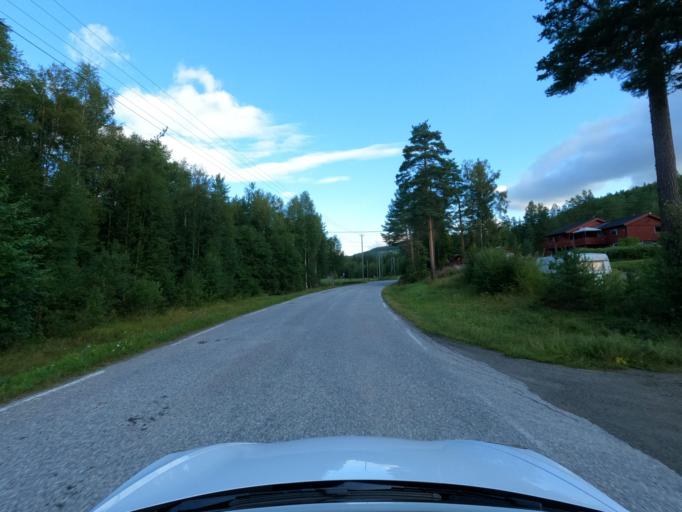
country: NO
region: Telemark
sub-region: Hjartdal
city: Sauland
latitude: 59.8256
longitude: 9.0634
